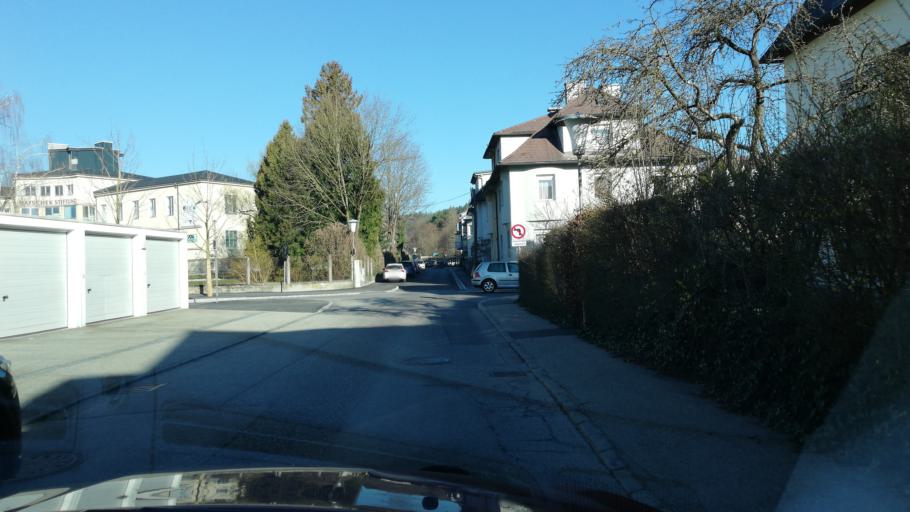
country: AT
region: Upper Austria
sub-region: Politischer Bezirk Vocklabruck
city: Vocklabruck
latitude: 48.0056
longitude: 13.6497
